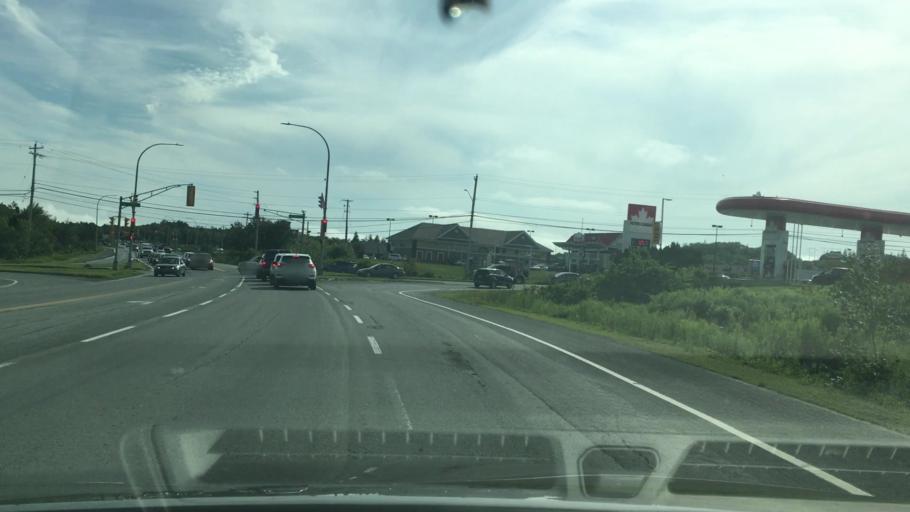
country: CA
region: Nova Scotia
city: Dartmouth
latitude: 44.7050
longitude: -63.8549
